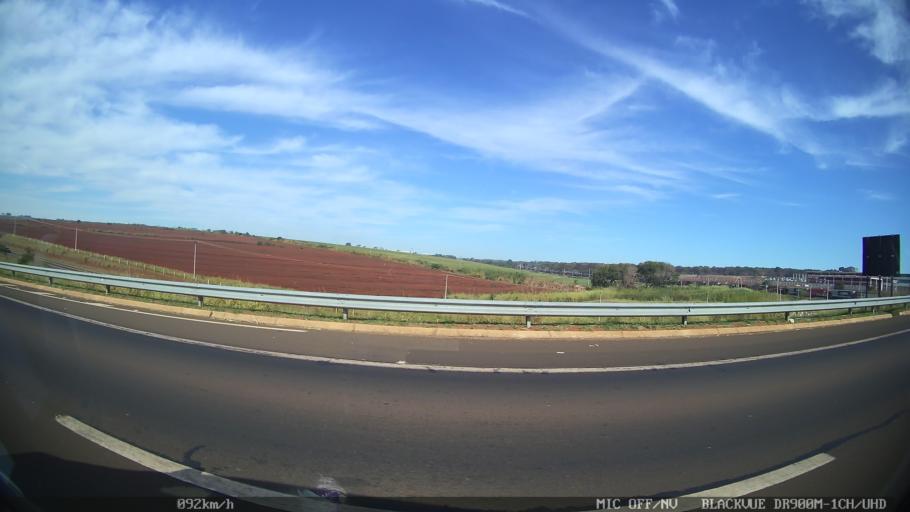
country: BR
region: Sao Paulo
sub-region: Araraquara
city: Araraquara
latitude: -21.7927
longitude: -48.1304
